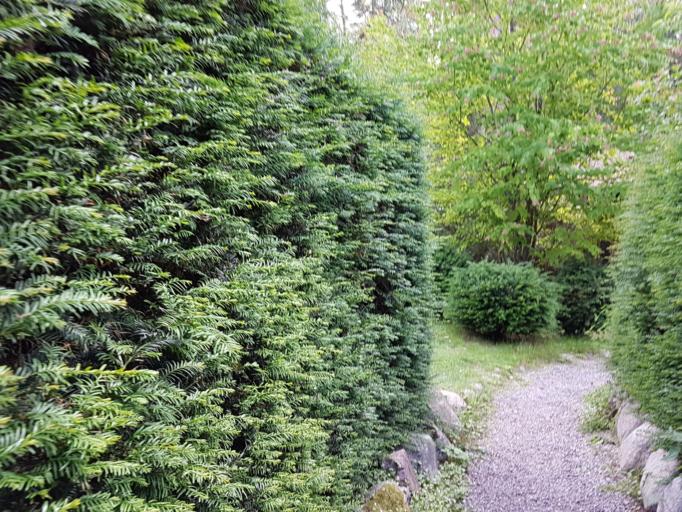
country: SE
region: Stockholm
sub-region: Lidingo
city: Brevik
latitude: 59.3453
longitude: 18.2393
